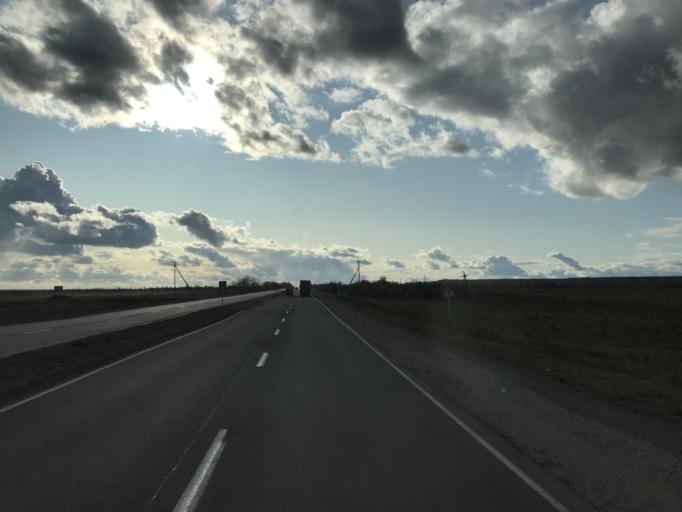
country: KZ
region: Qostanay
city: Rudnyy
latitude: 53.0129
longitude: 63.3085
